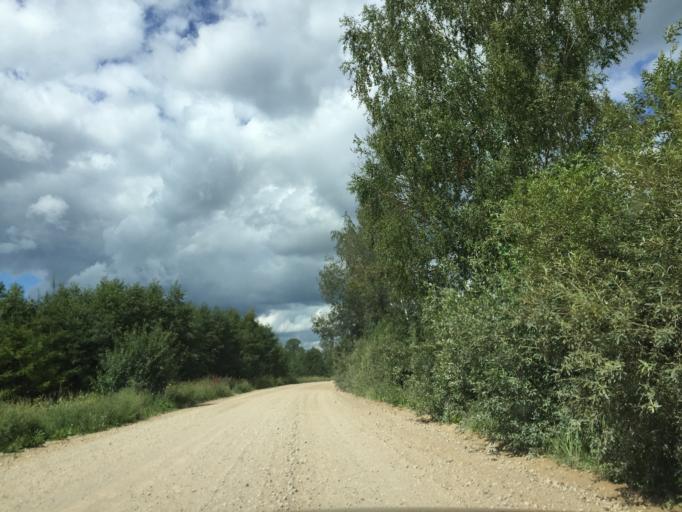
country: LV
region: Ropazu
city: Ropazi
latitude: 56.9059
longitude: 24.7801
